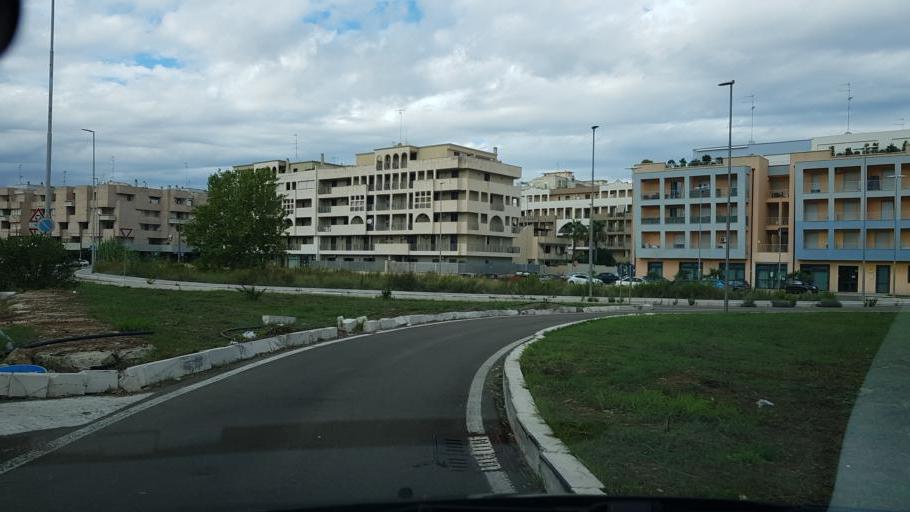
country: IT
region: Apulia
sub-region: Provincia di Lecce
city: Lecce
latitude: 40.3450
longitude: 18.1843
